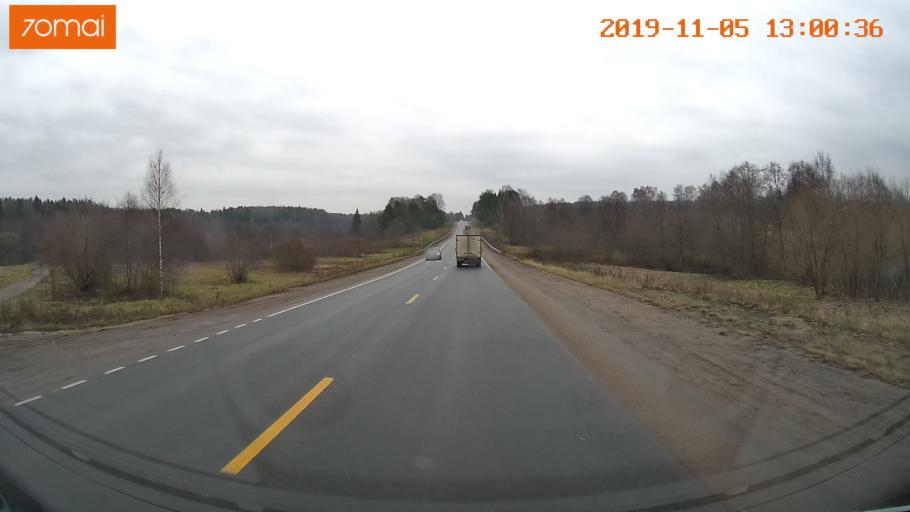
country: RU
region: Ivanovo
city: Kokhma
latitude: 56.9132
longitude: 41.1476
